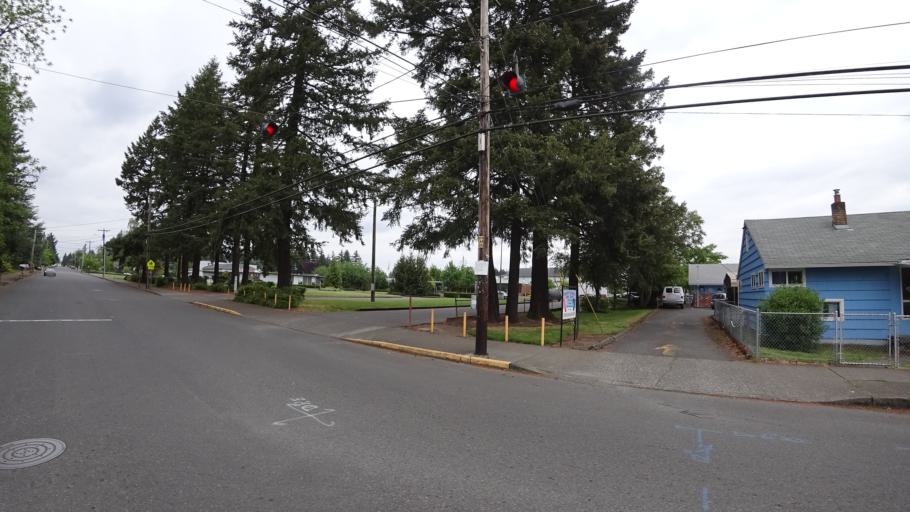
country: US
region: Oregon
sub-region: Multnomah County
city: Lents
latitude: 45.5116
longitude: -122.5300
